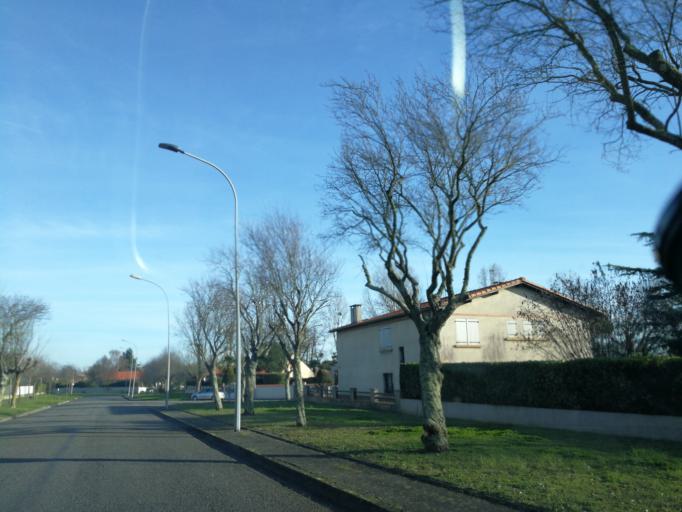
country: FR
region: Midi-Pyrenees
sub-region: Departement de la Haute-Garonne
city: L'Union
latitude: 43.6462
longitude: 1.4757
